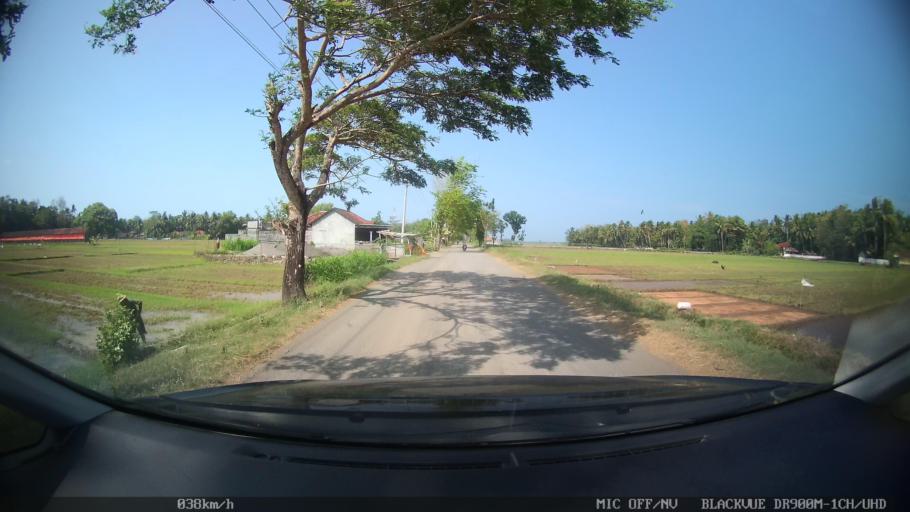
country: ID
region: Daerah Istimewa Yogyakarta
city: Srandakan
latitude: -7.9569
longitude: 110.2166
